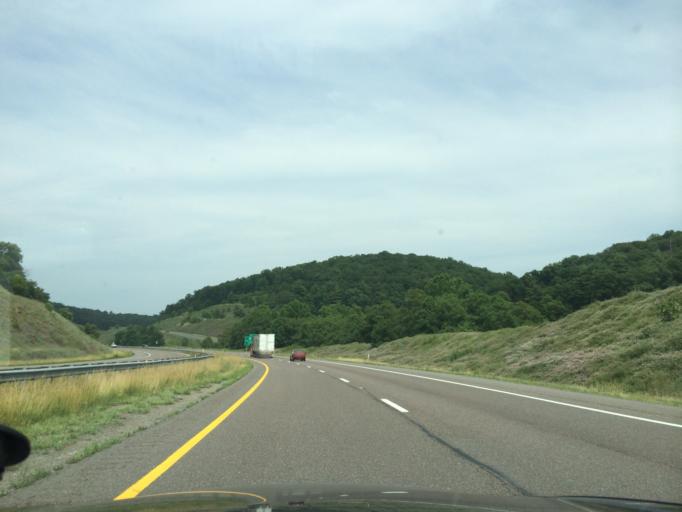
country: US
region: West Virginia
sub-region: Morgan County
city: Berkeley Springs
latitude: 39.7019
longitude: -78.3516
